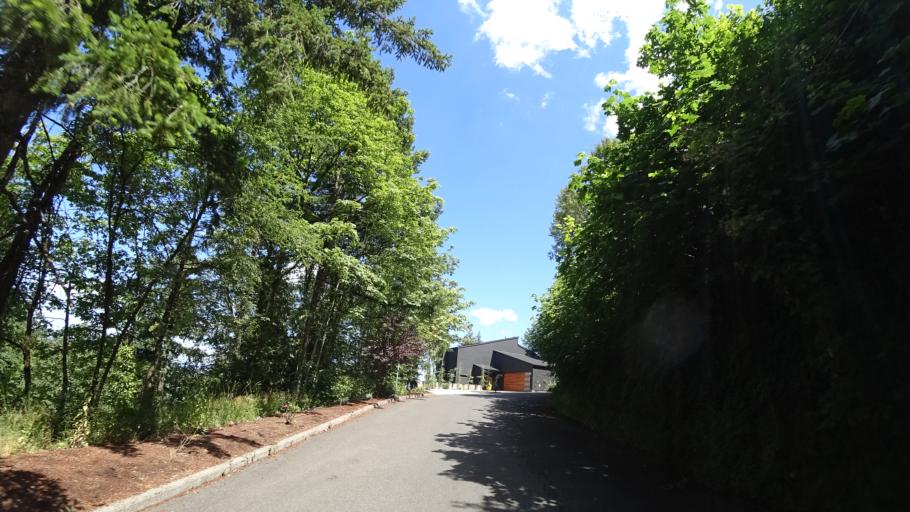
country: US
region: Oregon
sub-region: Multnomah County
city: Portland
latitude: 45.5103
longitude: -122.6917
